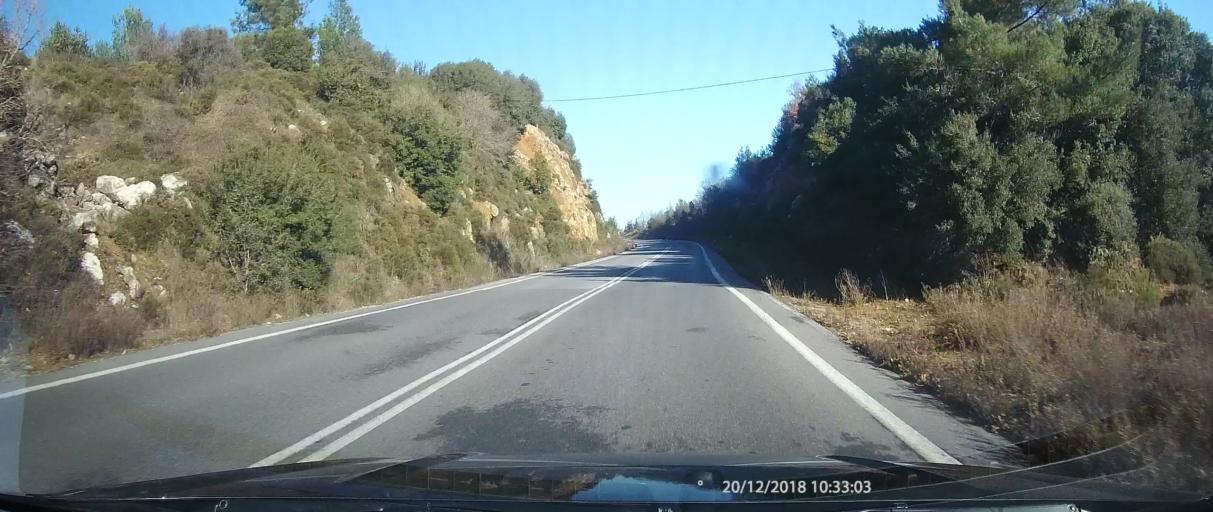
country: GR
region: Peloponnese
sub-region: Nomos Lakonias
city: Kariai
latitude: 37.3337
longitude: 22.4180
